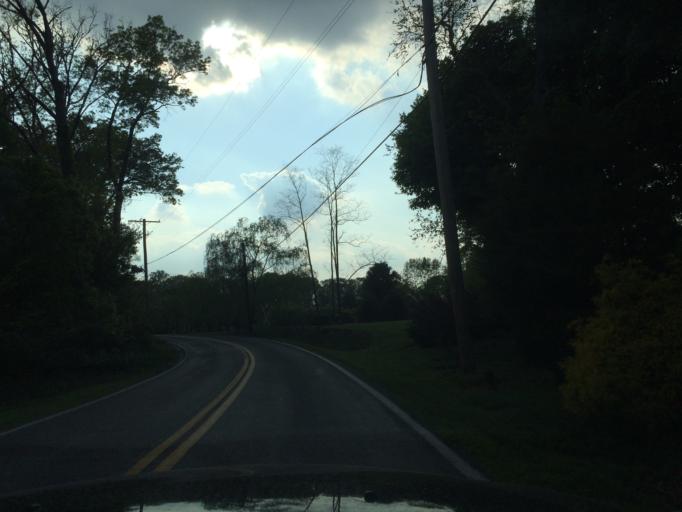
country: US
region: Maryland
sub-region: Carroll County
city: Mount Airy
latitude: 39.2941
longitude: -77.0731
